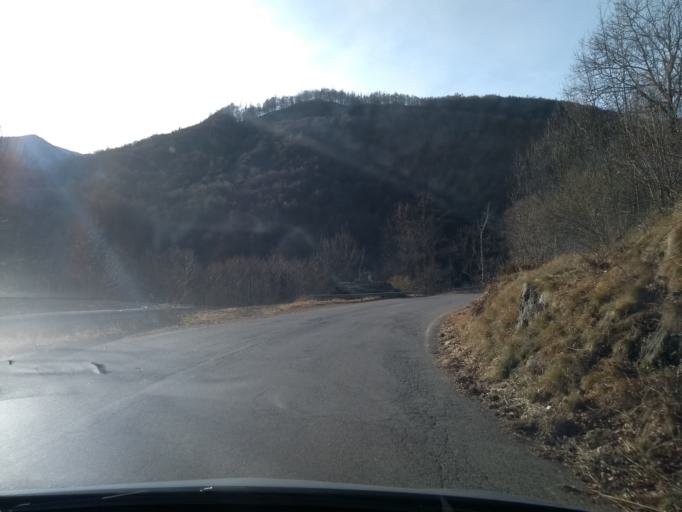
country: IT
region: Piedmont
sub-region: Provincia di Torino
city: Ala di Stura
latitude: 45.3117
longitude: 7.3225
